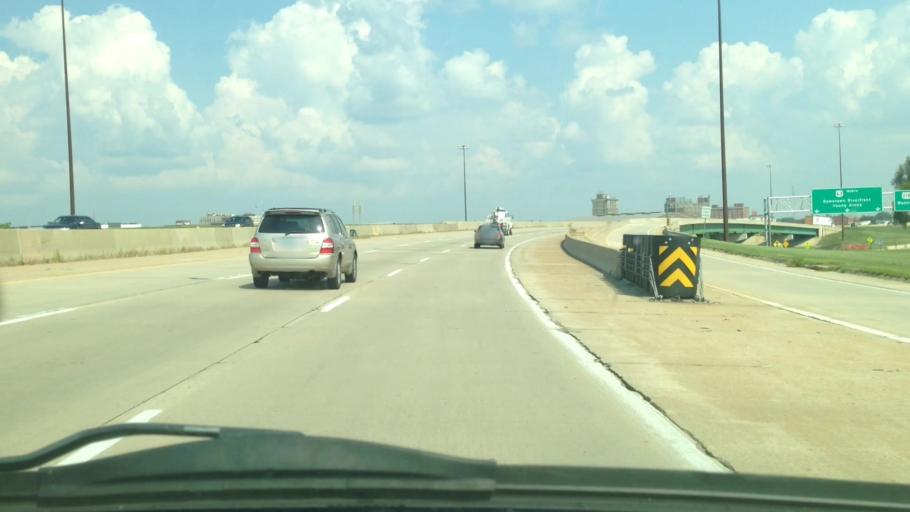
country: US
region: Iowa
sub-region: Black Hawk County
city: Waterloo
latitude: 42.4971
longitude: -92.3503
